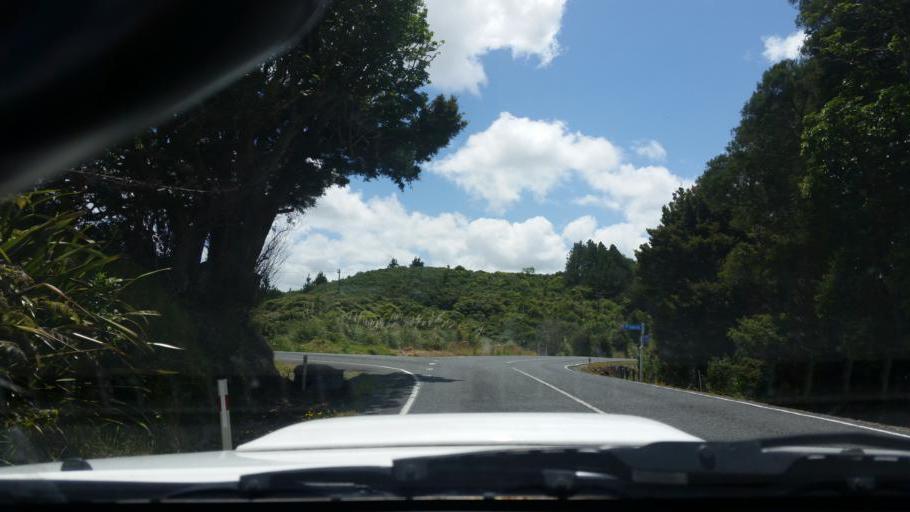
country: NZ
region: Northland
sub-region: Whangarei
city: Ruakaka
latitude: -36.0852
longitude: 174.2403
